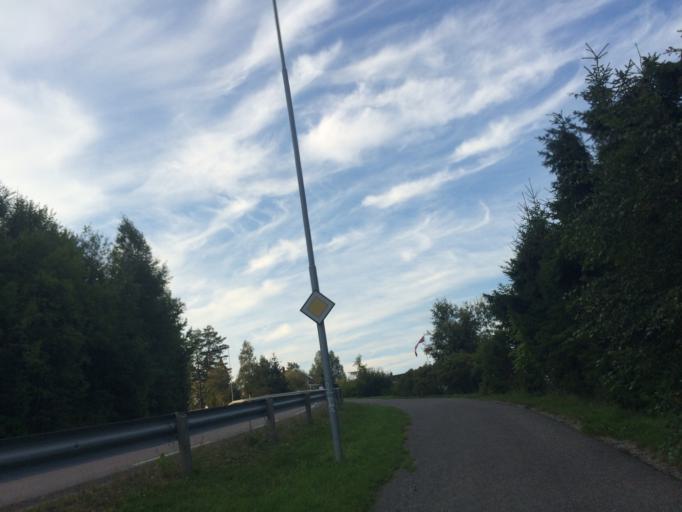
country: NO
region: Akershus
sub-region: Ski
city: Ski
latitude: 59.6741
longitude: 10.8868
